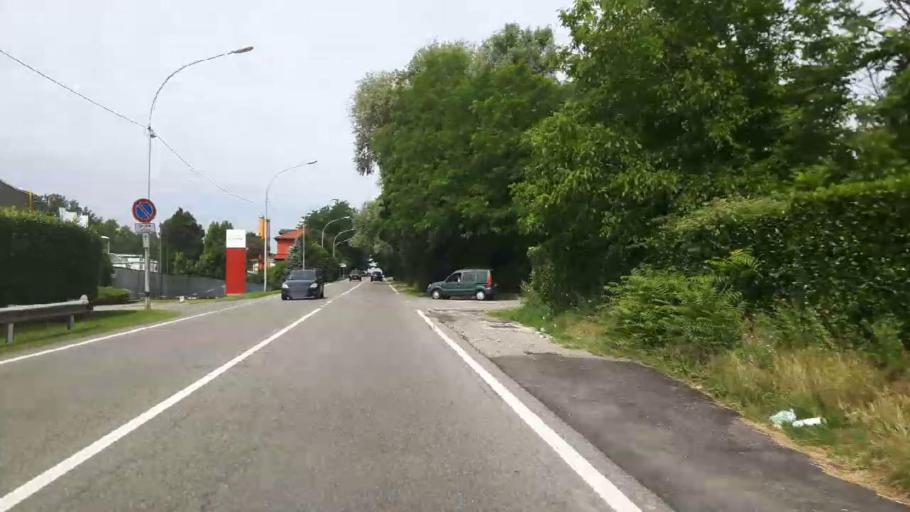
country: IT
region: Lombardy
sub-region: Provincia di Como
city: Grandate
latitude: 45.7839
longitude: 9.0647
